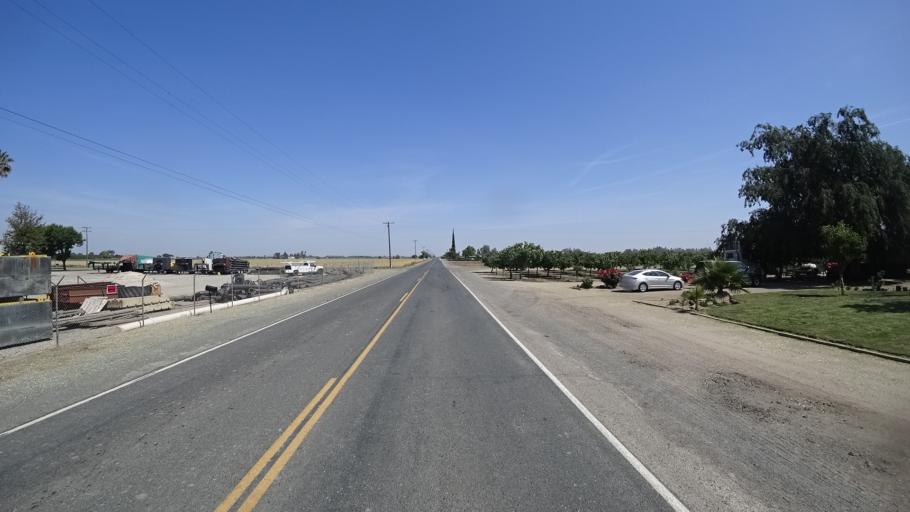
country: US
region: California
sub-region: Fresno County
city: Riverdale
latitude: 36.3941
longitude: -119.8513
